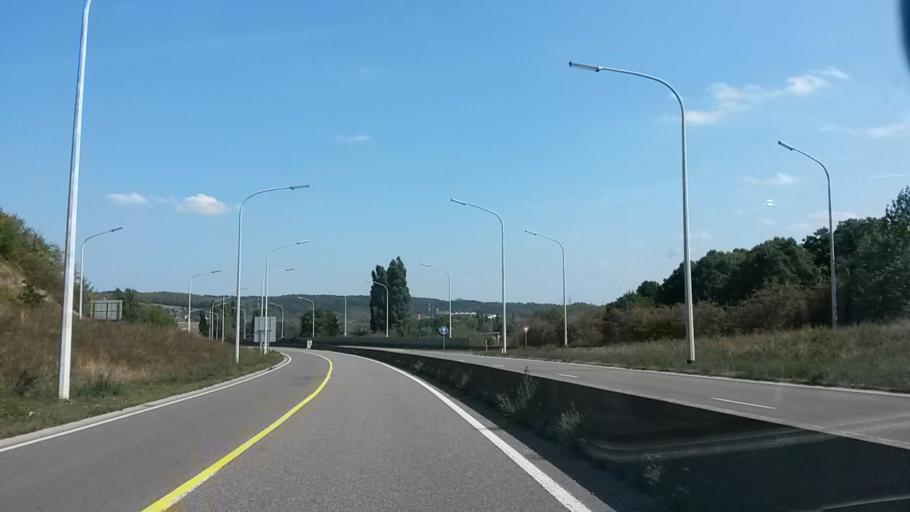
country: BE
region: Wallonia
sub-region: Province du Hainaut
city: Farciennes
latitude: 50.4328
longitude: 4.5400
